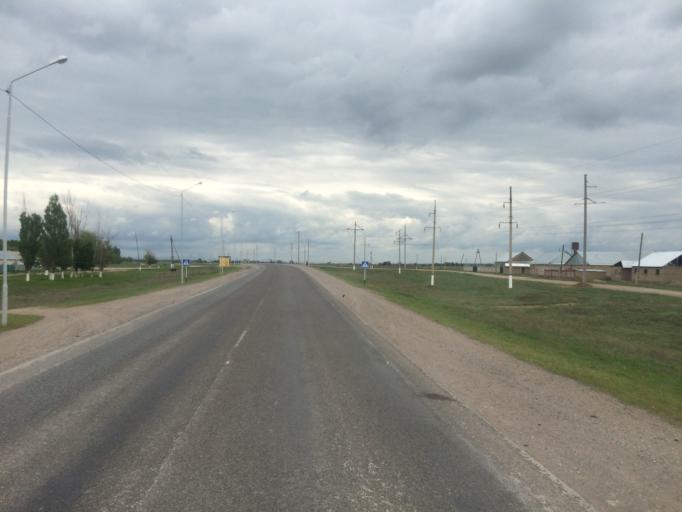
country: KG
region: Chuy
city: Sokuluk
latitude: 43.2472
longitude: 74.2976
